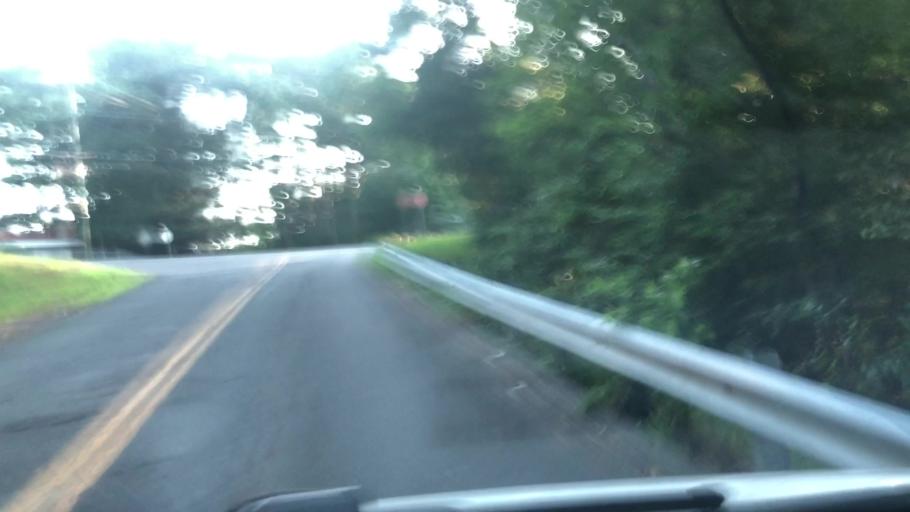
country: US
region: Massachusetts
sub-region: Hampshire County
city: Easthampton
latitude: 42.2820
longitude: -72.7140
